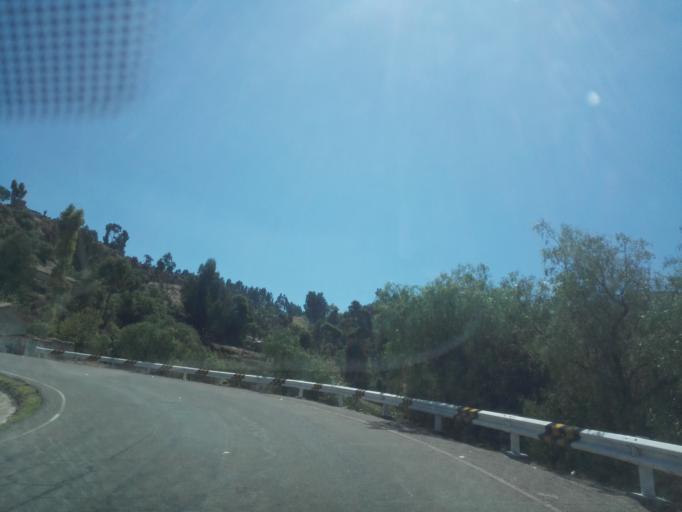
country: PE
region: Ayacucho
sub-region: Provincia de Huamanga
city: Ayacucho
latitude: -13.1650
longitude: -74.2444
